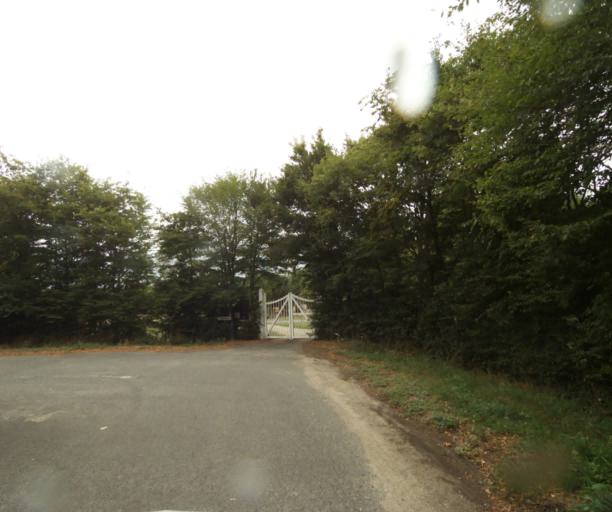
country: FR
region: Pays de la Loire
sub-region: Departement de la Sarthe
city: Sable-sur-Sarthe
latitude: 47.8212
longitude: -0.3692
